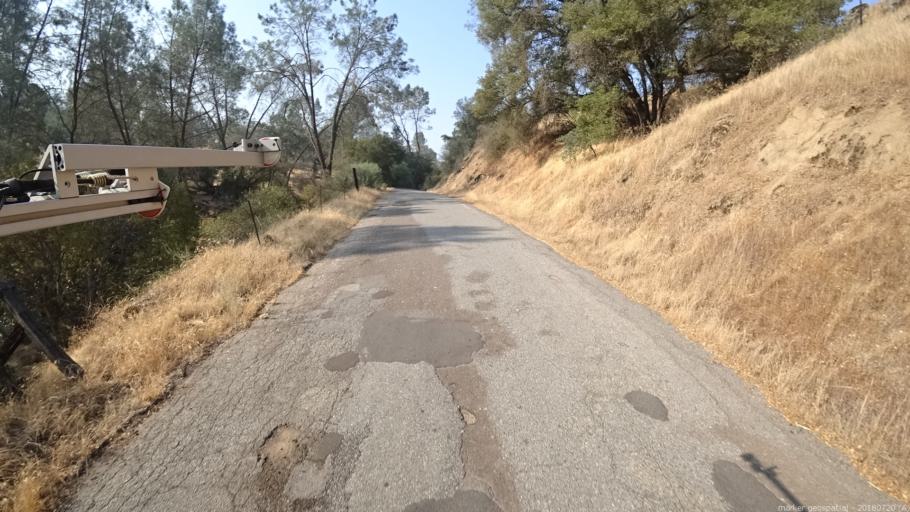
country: US
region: California
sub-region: Madera County
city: Yosemite Lakes
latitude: 37.2527
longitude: -119.8992
